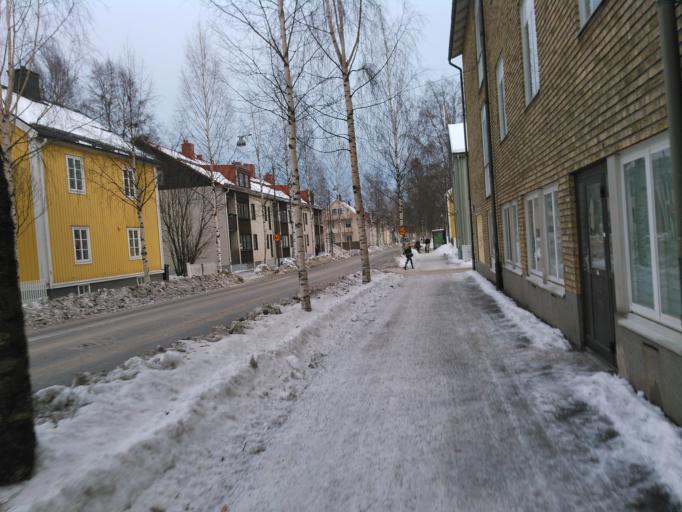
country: SE
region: Vaesterbotten
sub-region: Umea Kommun
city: Umea
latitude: 63.8305
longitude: 20.2410
